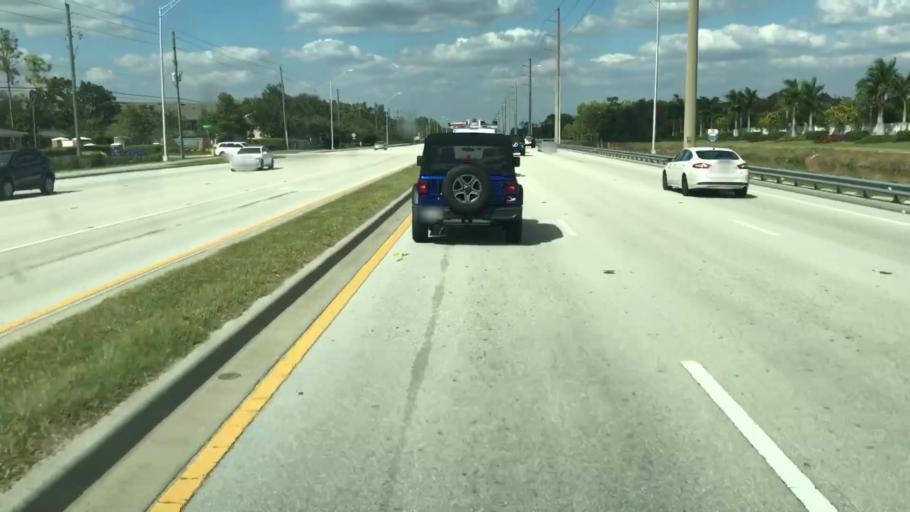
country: US
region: Florida
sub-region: Collier County
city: Vineyards
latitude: 26.2593
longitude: -81.6888
